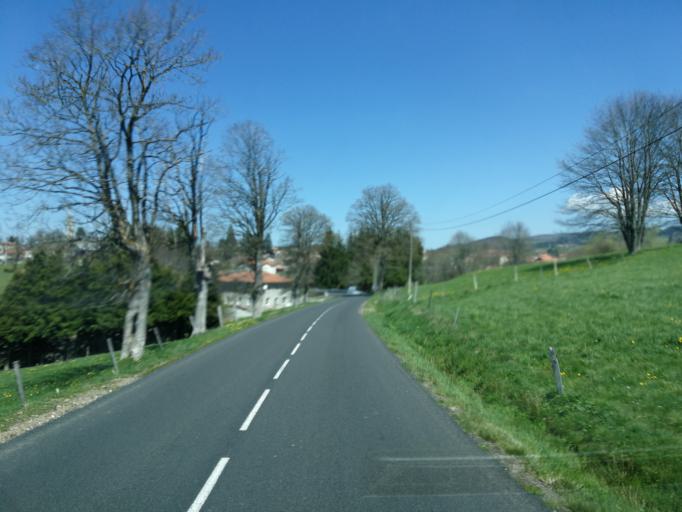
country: FR
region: Rhone-Alpes
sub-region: Departement de la Loire
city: Marlhes
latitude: 45.2779
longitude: 4.3950
